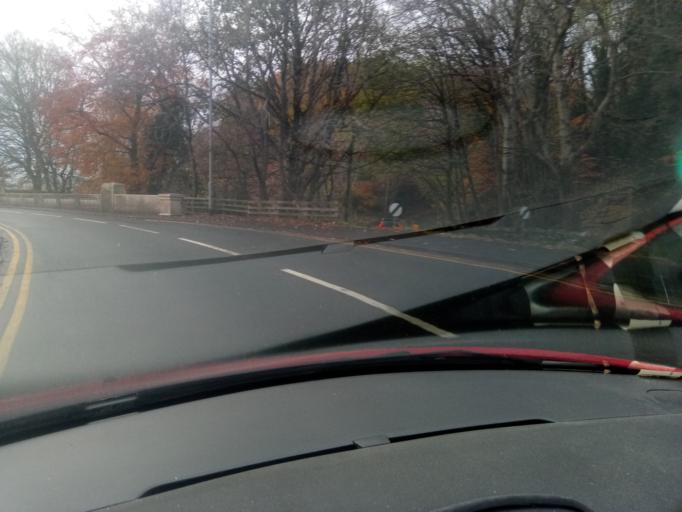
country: GB
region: Scotland
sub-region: The Scottish Borders
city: Jedburgh
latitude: 55.4850
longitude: -2.5450
